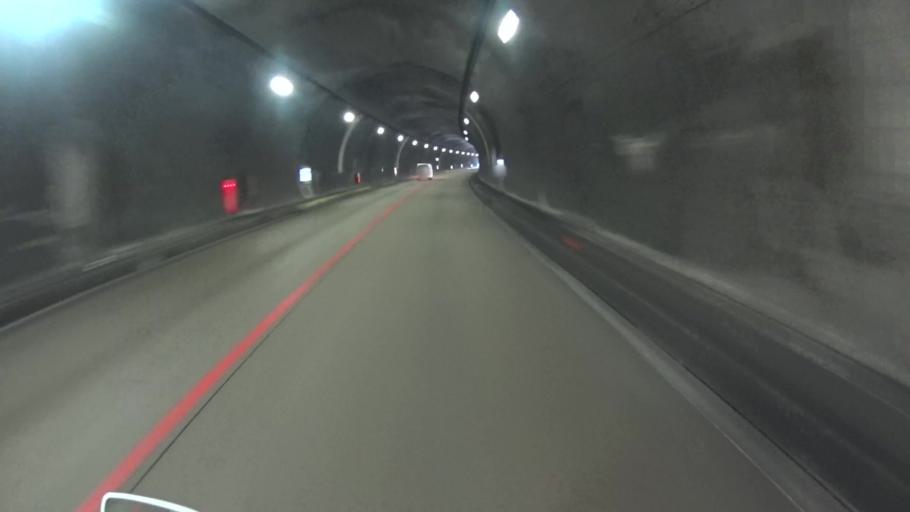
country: JP
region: Kyoto
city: Kameoka
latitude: 34.9948
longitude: 135.5738
